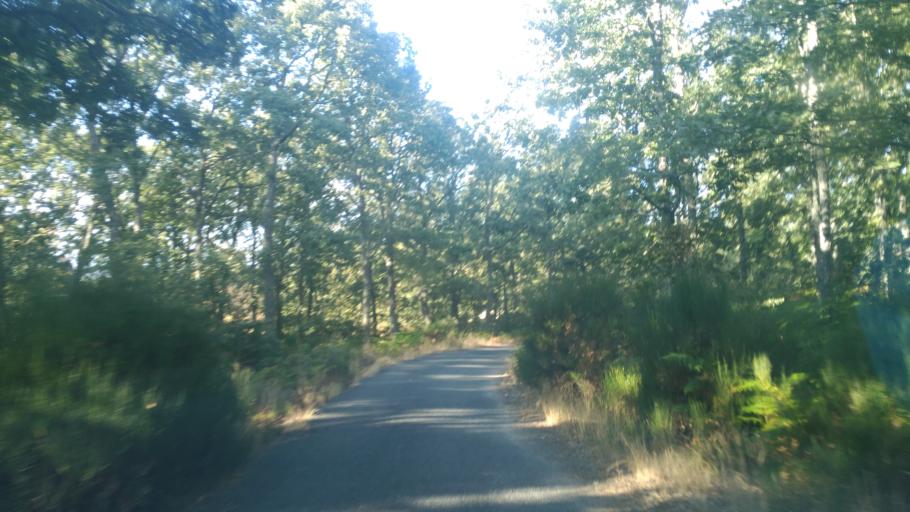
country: ES
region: Castille and Leon
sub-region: Provincia de Salamanca
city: Nava de Francia
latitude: 40.5233
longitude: -6.0962
